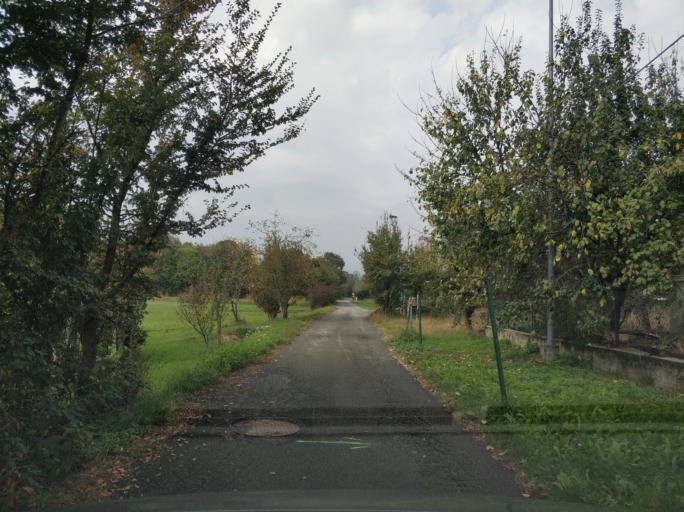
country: IT
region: Piedmont
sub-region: Provincia di Torino
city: Grosso
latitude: 45.2572
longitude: 7.5727
